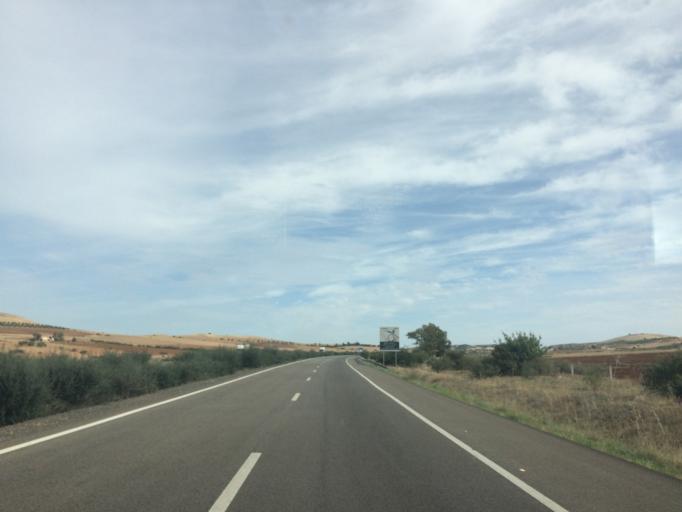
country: MA
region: Rabat-Sale-Zemmour-Zaer
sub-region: Khemisset
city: Khemisset
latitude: 33.7977
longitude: -5.8823
